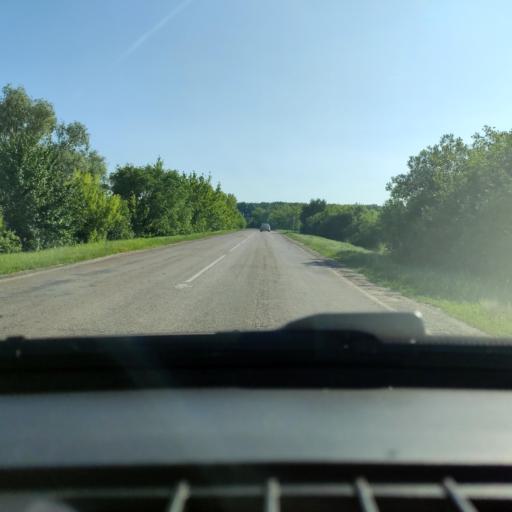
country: RU
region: Voronezj
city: Panino
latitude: 51.6001
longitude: 39.9802
